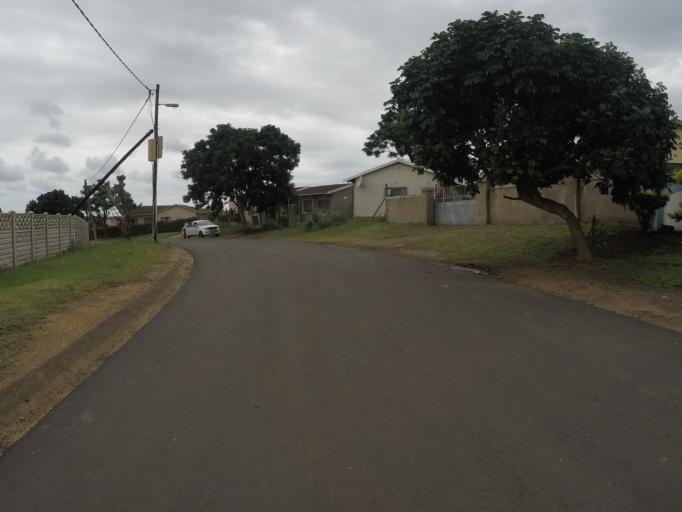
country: ZA
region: KwaZulu-Natal
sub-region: uThungulu District Municipality
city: Empangeni
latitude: -28.7839
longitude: 31.8515
